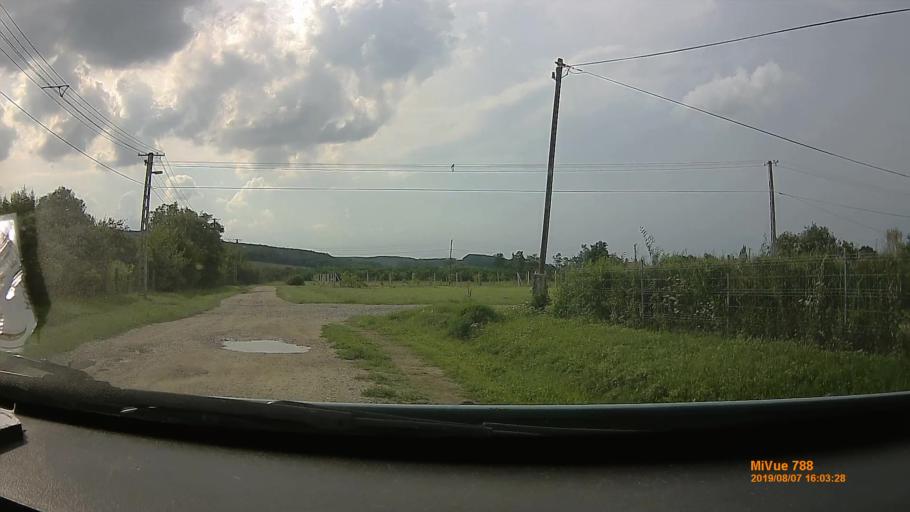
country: HU
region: Borsod-Abauj-Zemplen
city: Gonc
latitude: 48.4987
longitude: 21.2252
